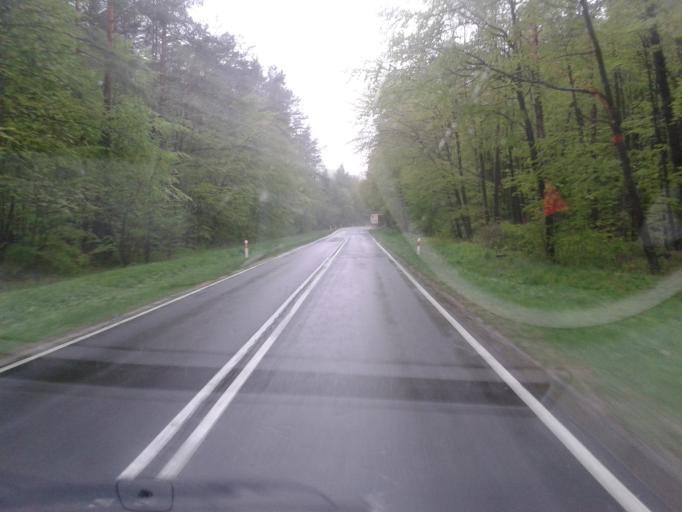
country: PL
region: Subcarpathian Voivodeship
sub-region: Powiat lubaczowski
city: Narol
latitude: 50.3407
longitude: 23.3092
